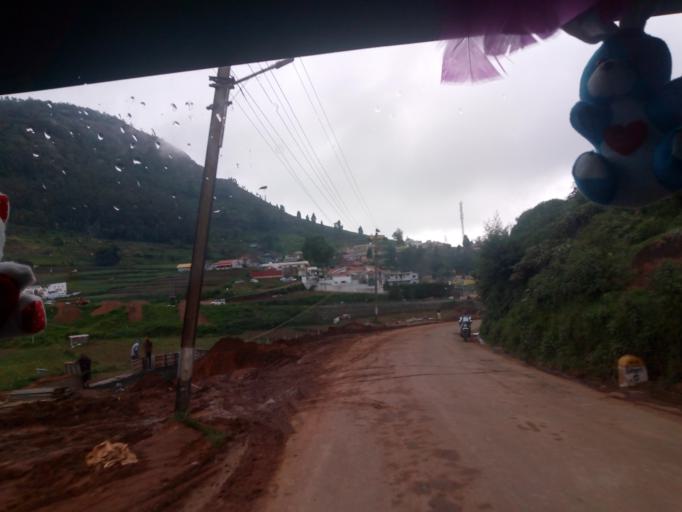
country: IN
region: Tamil Nadu
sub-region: Nilgiri
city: Ooty
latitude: 11.3976
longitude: 76.7176
